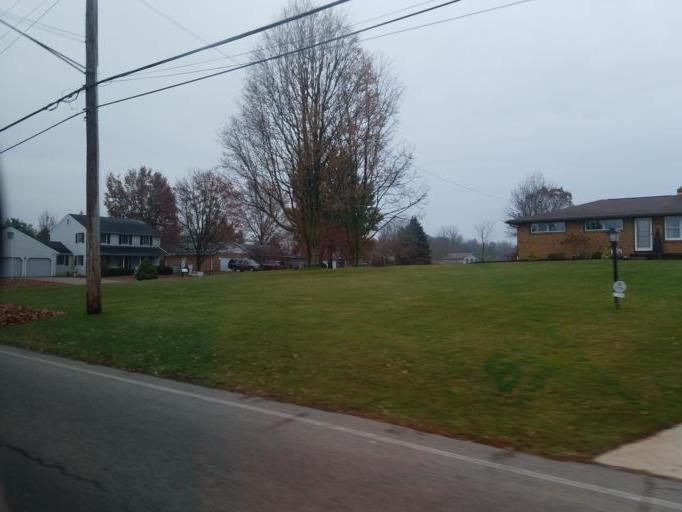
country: US
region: Ohio
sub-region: Richland County
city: Lexington
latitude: 40.6990
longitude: -82.5361
